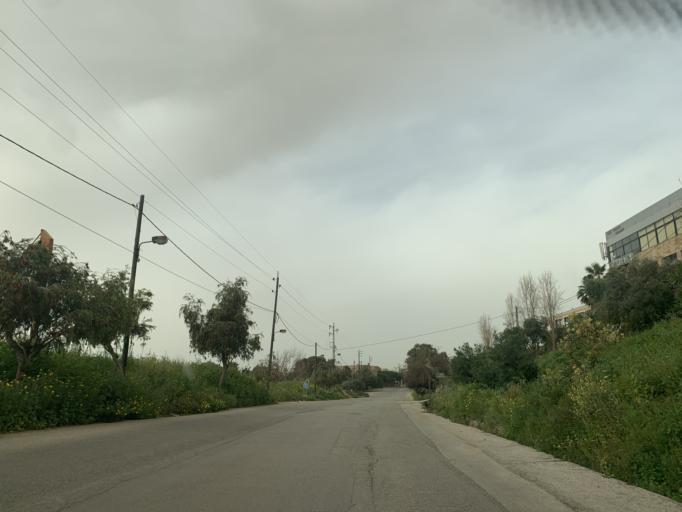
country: LB
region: Mont-Liban
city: Jbail
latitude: 34.1072
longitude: 35.6517
